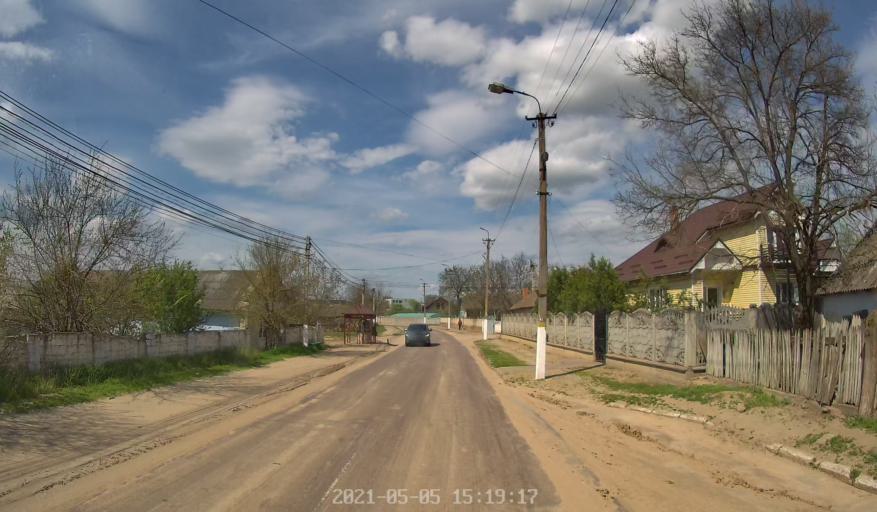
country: MD
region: Criuleni
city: Criuleni
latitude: 47.1258
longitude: 29.1940
